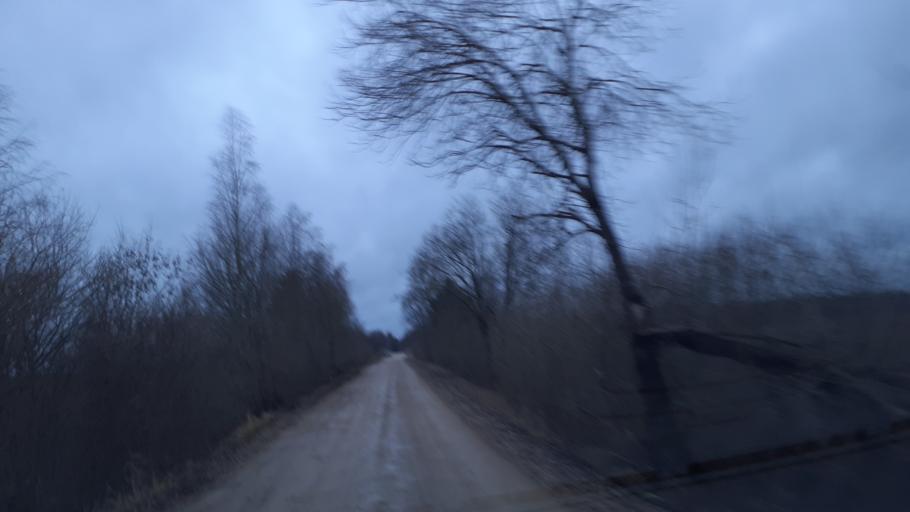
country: LV
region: Kuldigas Rajons
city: Kuldiga
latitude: 57.0448
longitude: 22.1338
